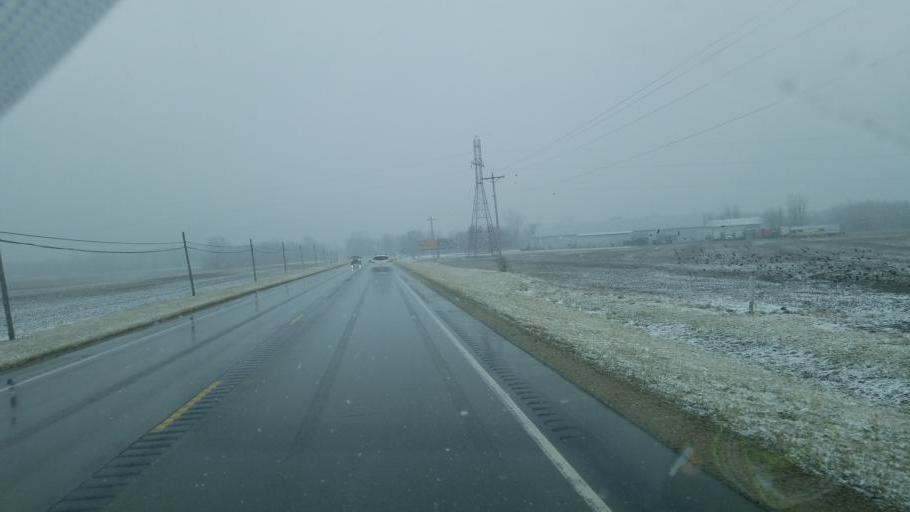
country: US
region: Indiana
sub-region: Grant County
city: Marion
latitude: 40.6220
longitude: -85.6993
